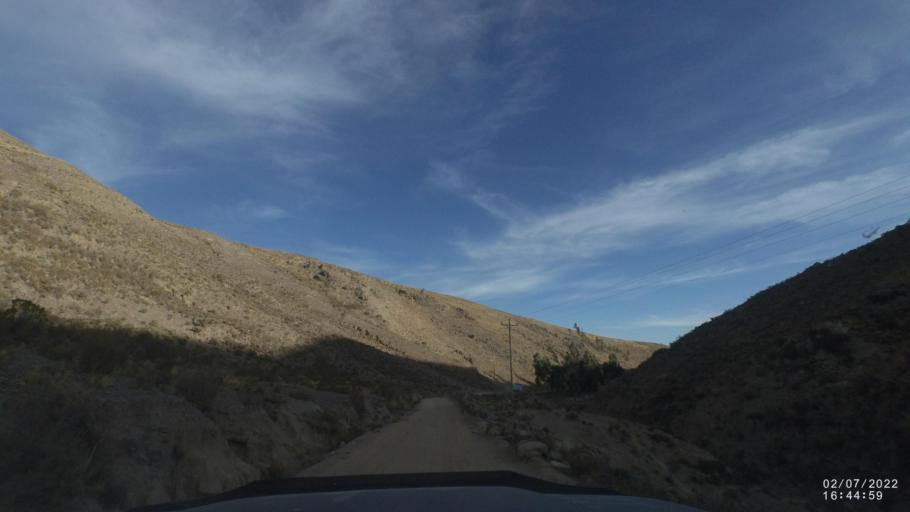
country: BO
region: Cochabamba
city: Irpa Irpa
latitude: -17.9740
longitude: -66.5097
